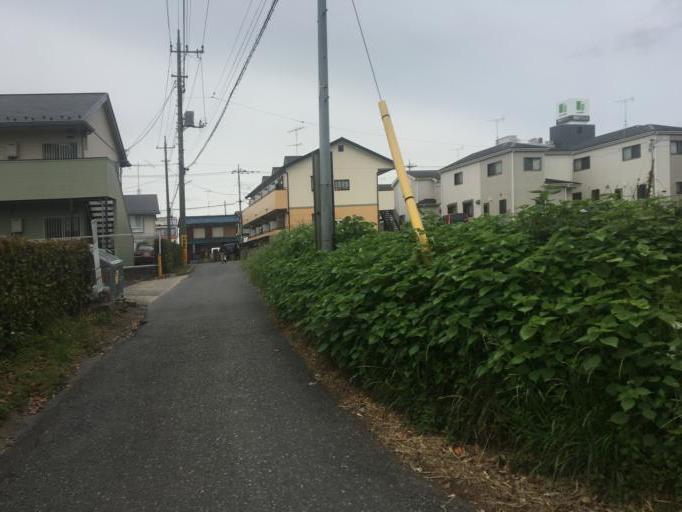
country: JP
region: Saitama
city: Fukiage-fujimi
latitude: 36.0411
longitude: 139.4137
